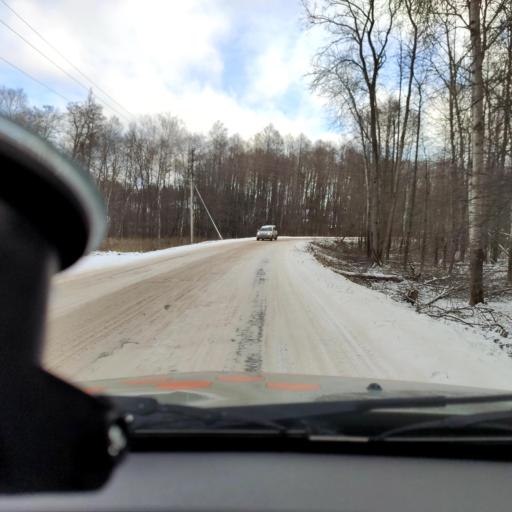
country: RU
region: Bashkortostan
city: Avdon
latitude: 54.7819
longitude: 55.7484
